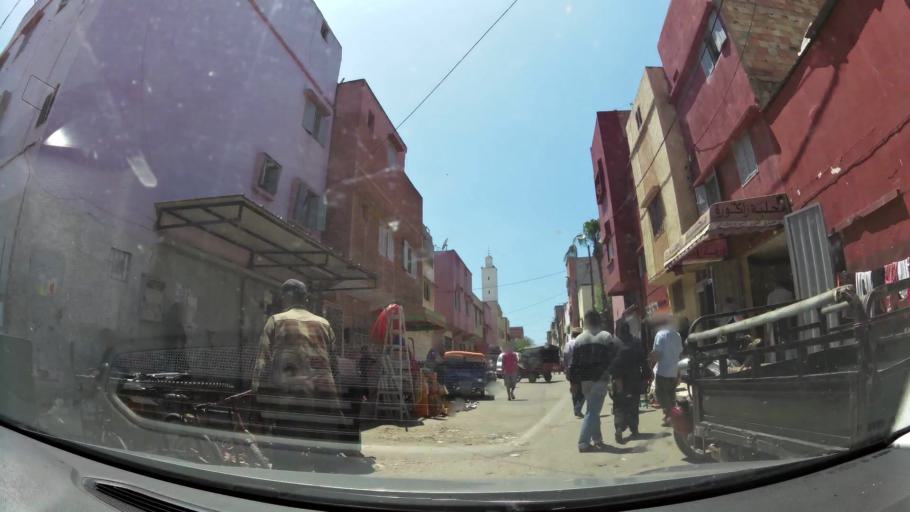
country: MA
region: Gharb-Chrarda-Beni Hssen
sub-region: Kenitra Province
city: Kenitra
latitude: 34.2567
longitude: -6.5583
